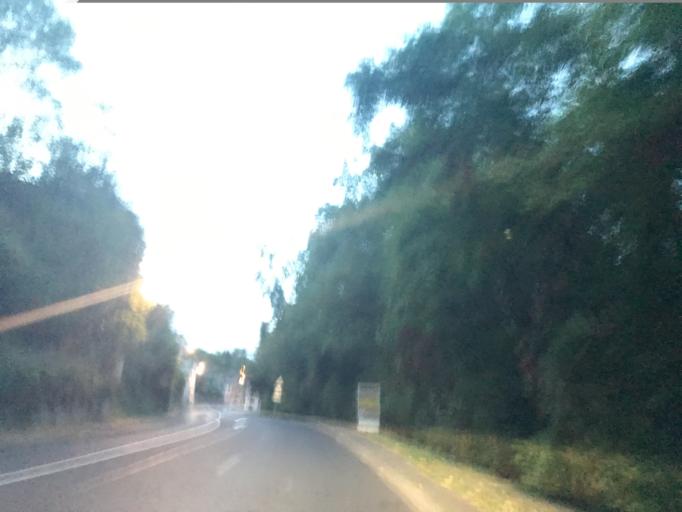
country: FR
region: Auvergne
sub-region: Departement du Puy-de-Dome
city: Thiers
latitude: 45.8559
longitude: 3.5372
